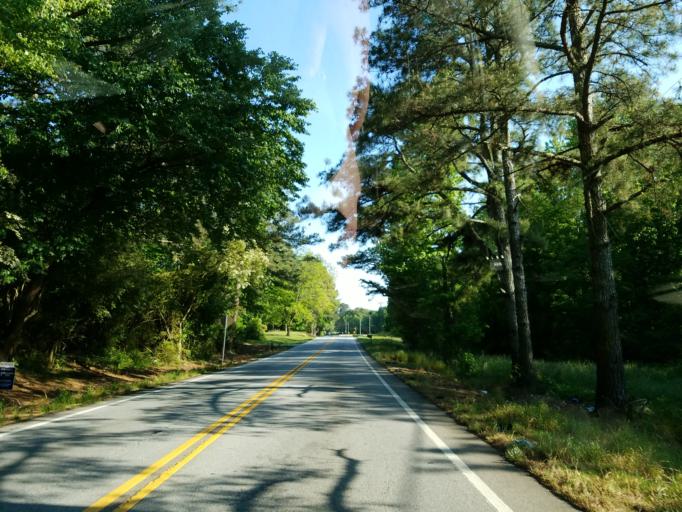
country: US
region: Georgia
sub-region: Carroll County
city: Temple
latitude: 33.8241
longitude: -84.9769
